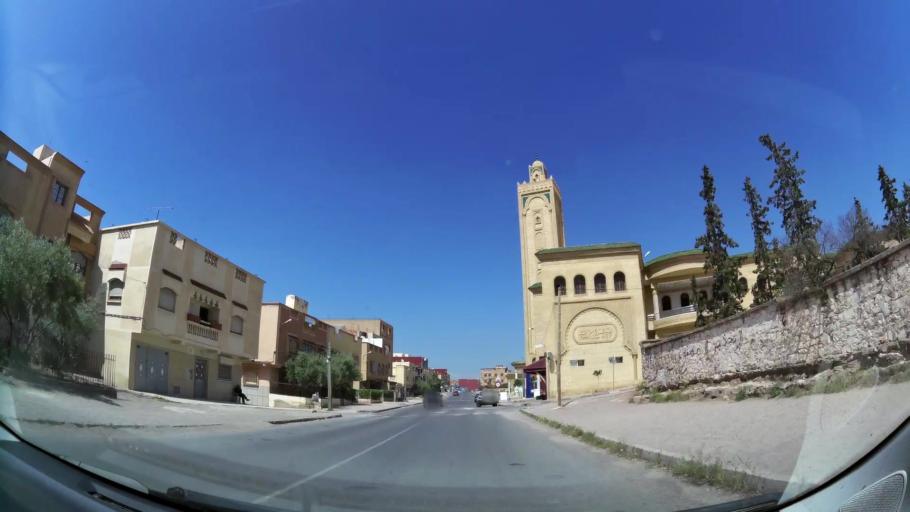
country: MA
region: Oriental
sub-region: Oujda-Angad
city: Oujda
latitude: 34.6877
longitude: -1.8795
